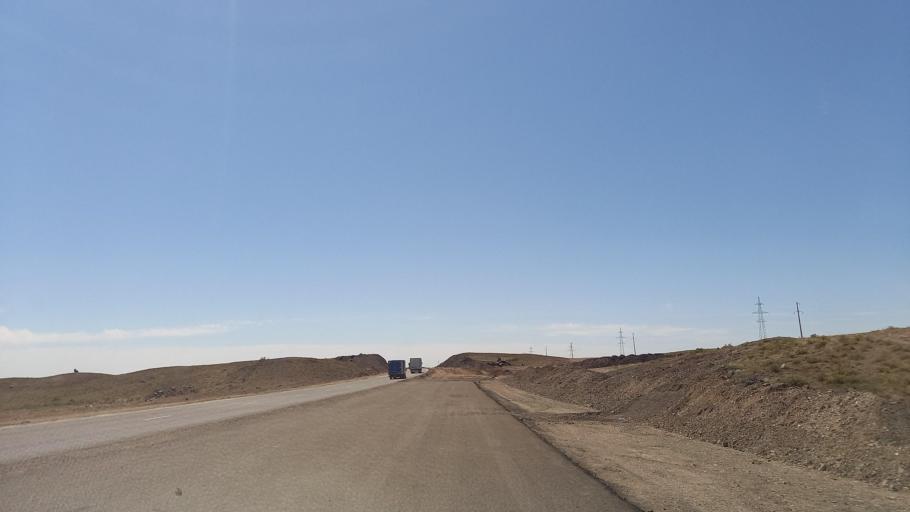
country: KZ
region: Zhambyl
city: Mynaral
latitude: 45.2847
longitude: 73.7750
